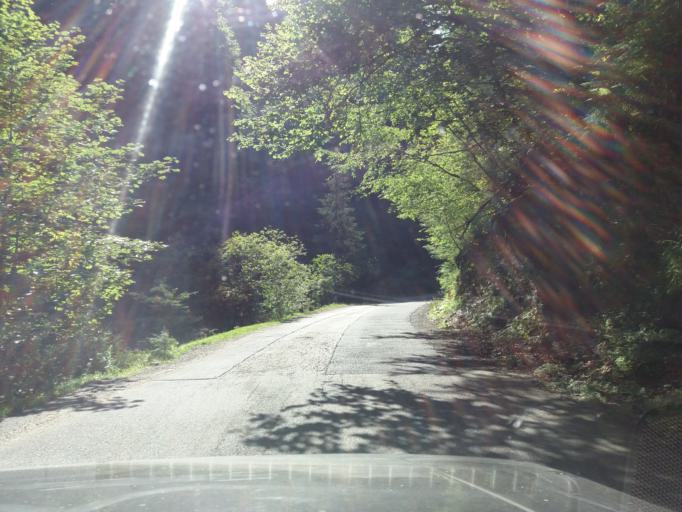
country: RO
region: Hunedoara
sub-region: Oras Petrila
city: Petrila
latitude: 45.4139
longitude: 23.4722
